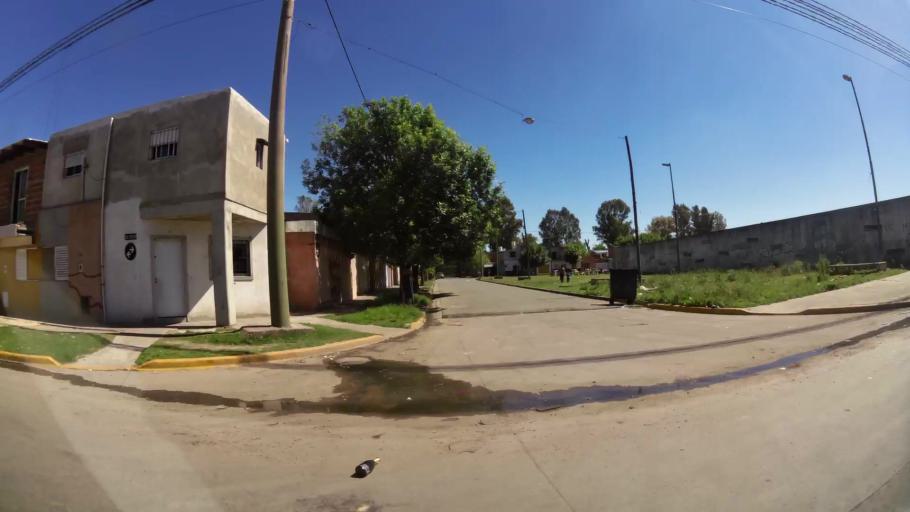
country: AR
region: Santa Fe
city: Perez
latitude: -32.9709
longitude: -60.7093
